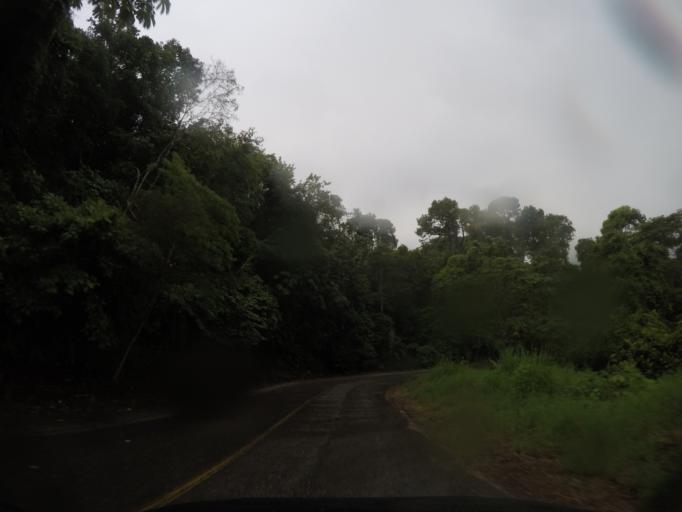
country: MX
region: Oaxaca
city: San Gabriel Mixtepec
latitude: 16.0805
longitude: -97.0844
